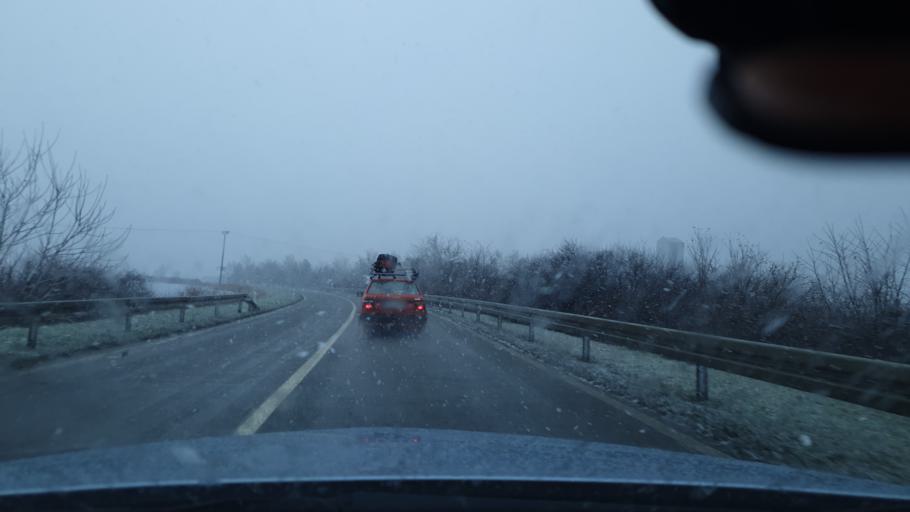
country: RS
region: Autonomna Pokrajina Vojvodina
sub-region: Juznobanatski Okrug
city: Pancevo
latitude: 44.8619
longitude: 20.7406
